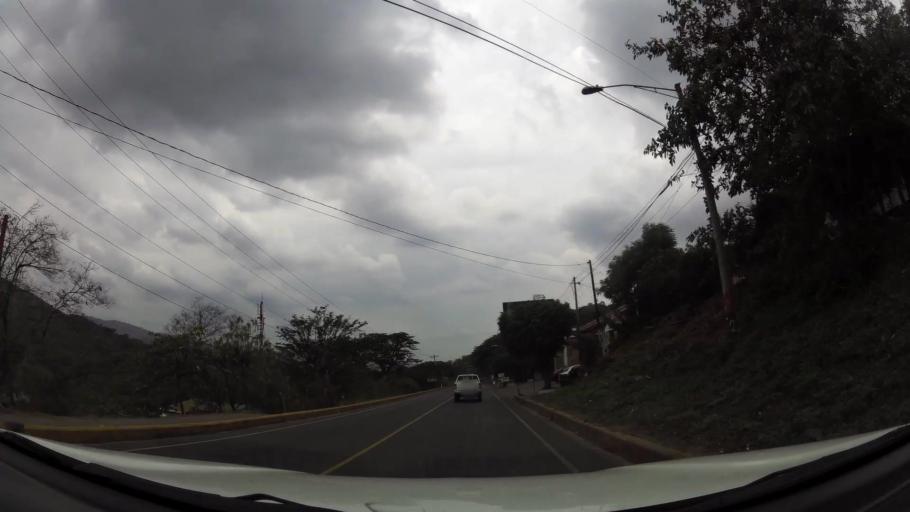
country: NI
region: Matagalpa
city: Matagalpa
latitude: 12.9196
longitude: -85.9330
